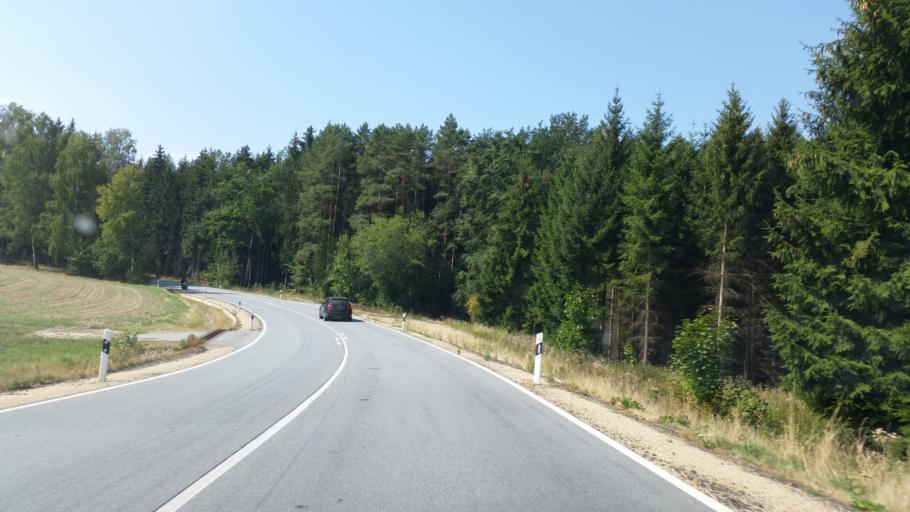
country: DE
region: Saxony
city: Grosshennersdorf
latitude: 50.9801
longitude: 14.7566
